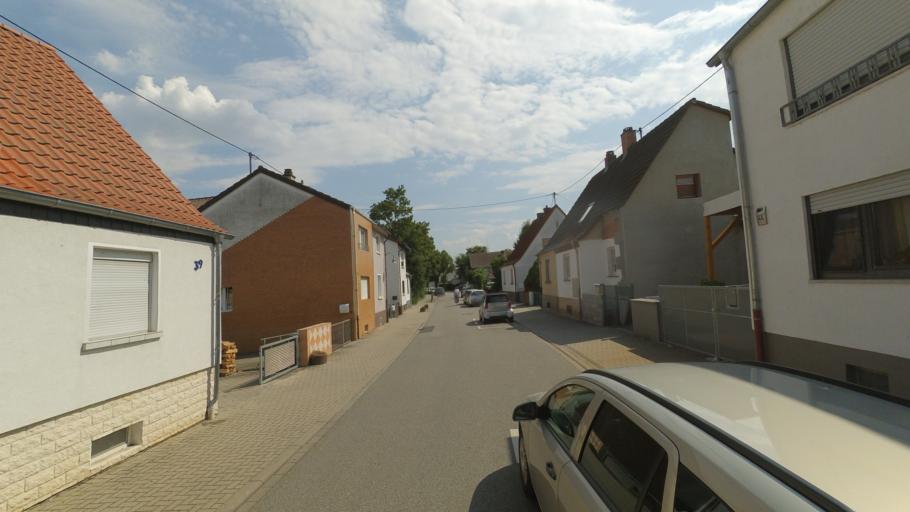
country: DE
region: Rheinland-Pfalz
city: Frankenthal
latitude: 49.5333
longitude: 8.3812
